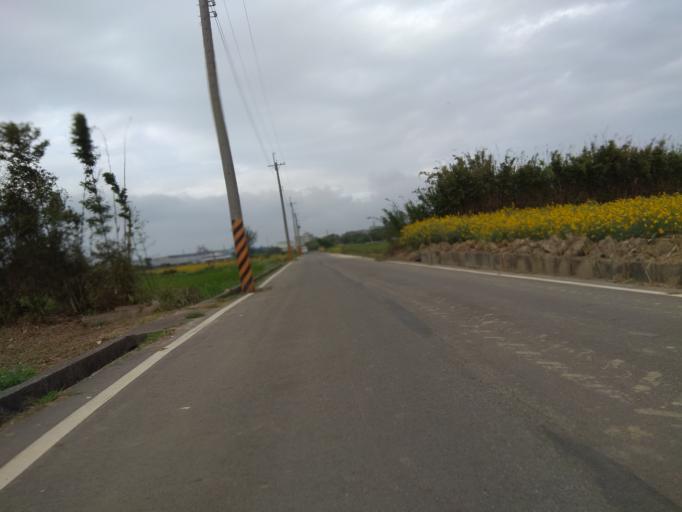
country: TW
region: Taiwan
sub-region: Hsinchu
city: Zhubei
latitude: 24.9752
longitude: 121.0376
